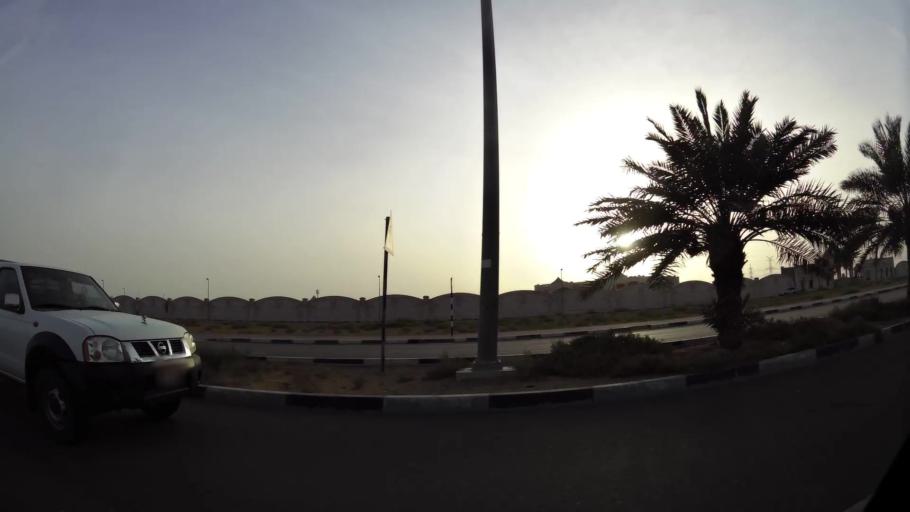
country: OM
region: Al Buraimi
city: Al Buraymi
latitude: 24.2707
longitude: 55.7205
